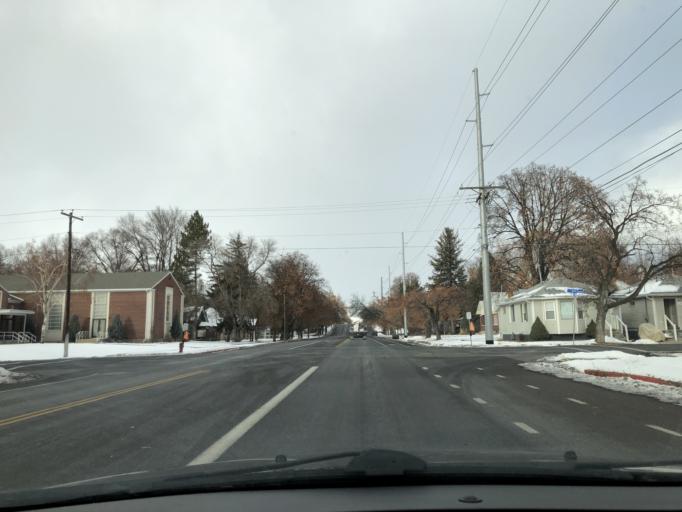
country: US
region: Utah
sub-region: Cache County
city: Logan
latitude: 41.7274
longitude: -111.8325
